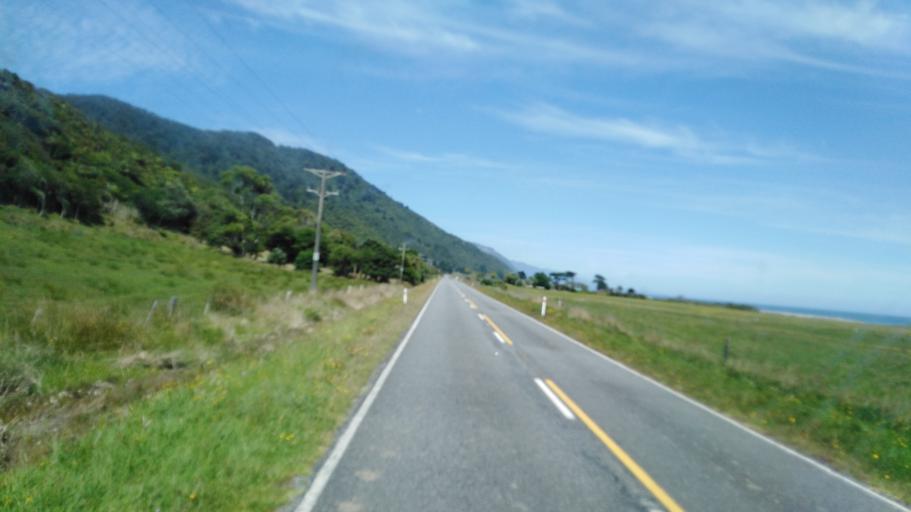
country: NZ
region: West Coast
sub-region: Buller District
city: Westport
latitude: -41.5521
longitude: 171.9214
